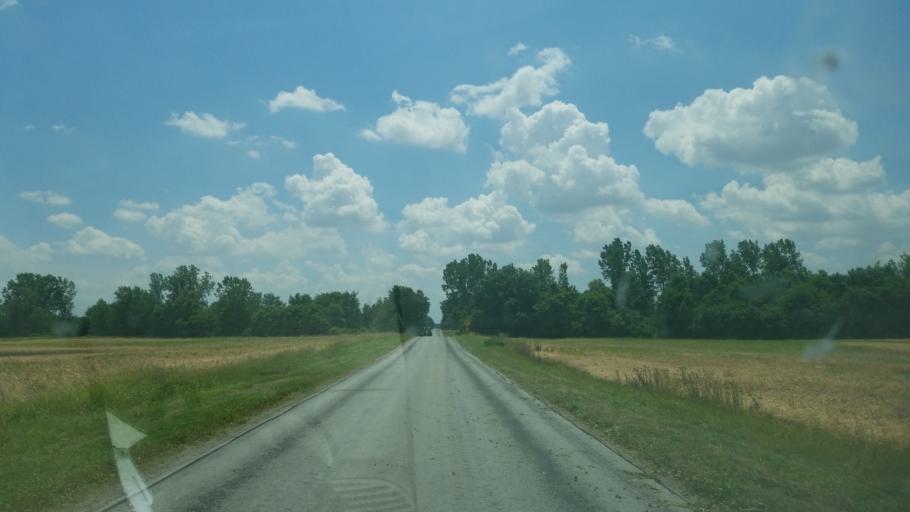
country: US
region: Ohio
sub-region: Hardin County
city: Kenton
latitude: 40.6276
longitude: -83.5609
